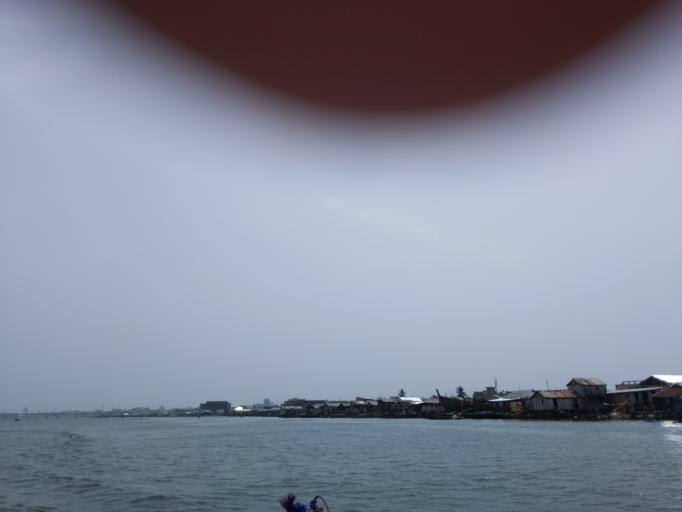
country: BJ
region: Littoral
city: Cotonou
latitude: 6.3857
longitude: 2.4350
